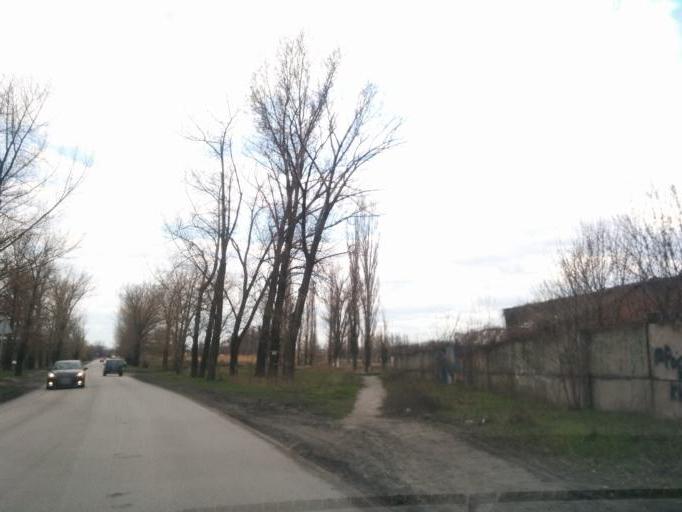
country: RU
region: Rostov
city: Shakhty
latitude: 47.6825
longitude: 40.2838
